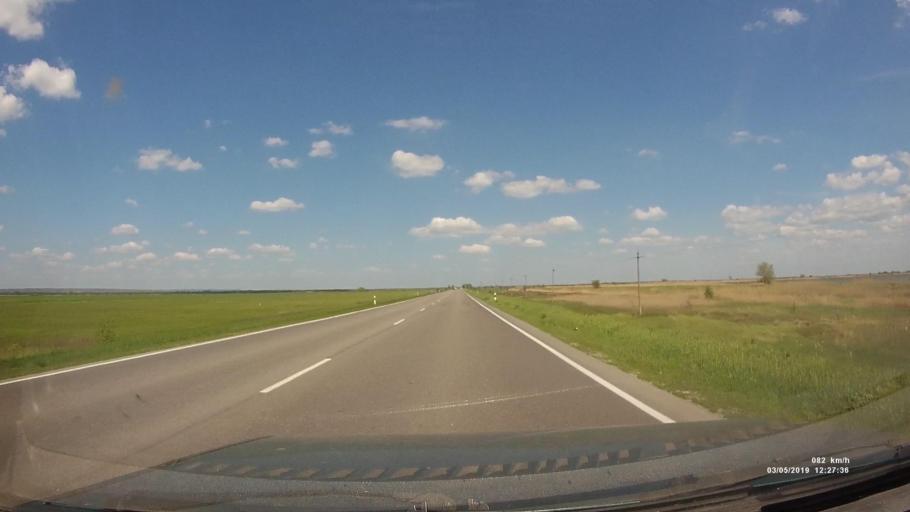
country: RU
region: Rostov
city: Semikarakorsk
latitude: 47.4612
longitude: 40.7220
